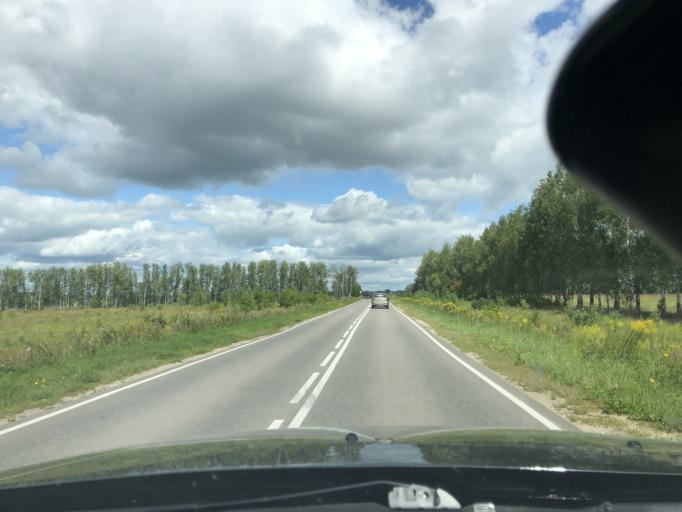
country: RU
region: Tula
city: Yasnogorsk
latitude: 54.4593
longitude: 37.7095
